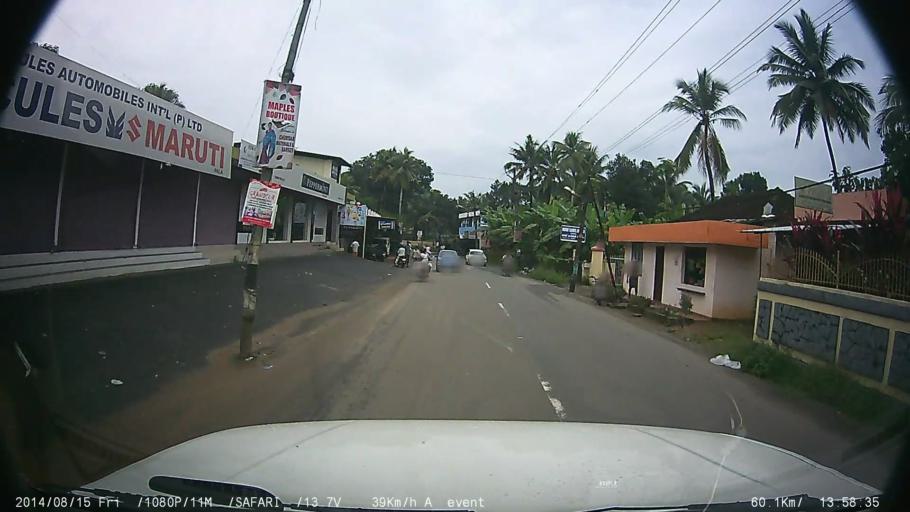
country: IN
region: Kerala
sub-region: Kottayam
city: Lalam
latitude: 9.7109
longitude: 76.6714
